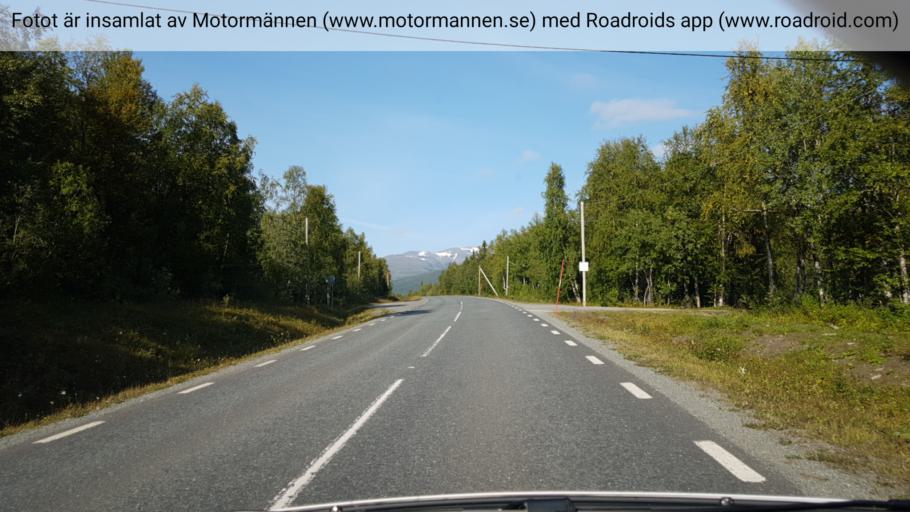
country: NO
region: Nordland
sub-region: Rana
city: Mo i Rana
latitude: 65.7571
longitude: 15.1146
